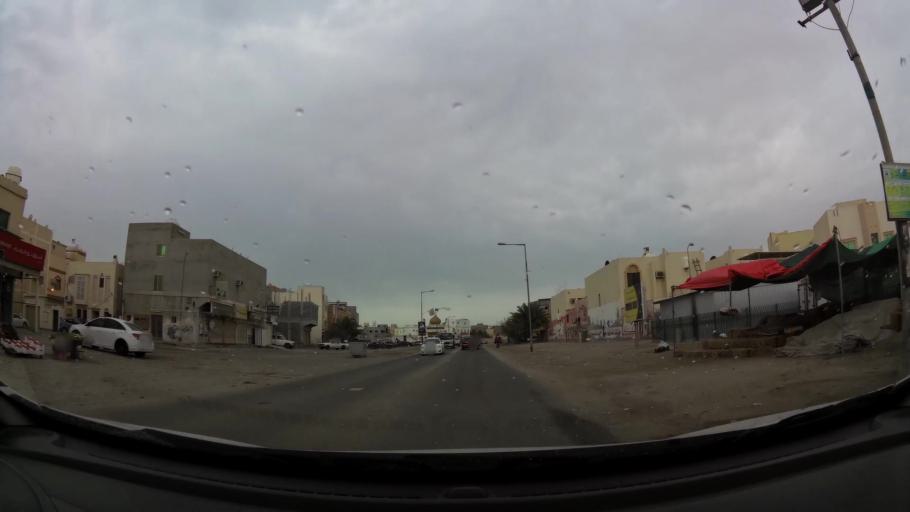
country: BH
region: Central Governorate
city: Madinat Hamad
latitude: 26.1260
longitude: 50.4775
